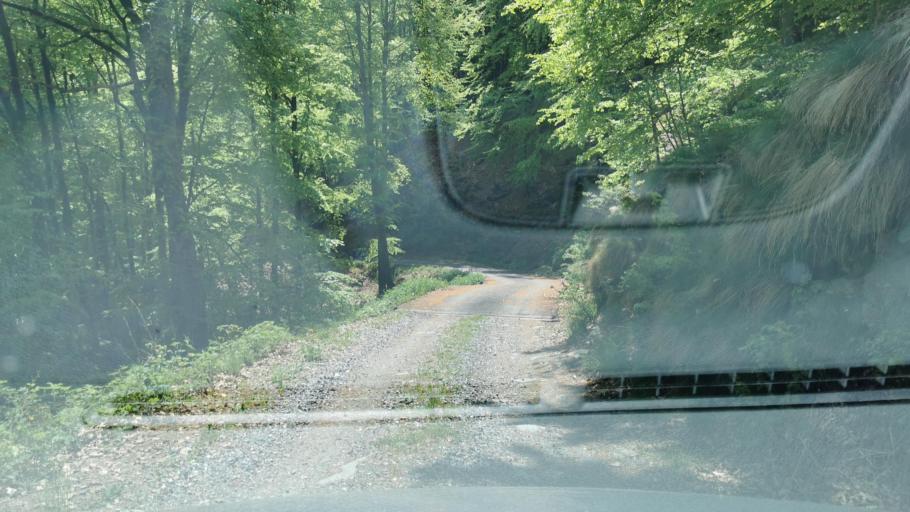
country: IT
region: Piedmont
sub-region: Provincia di Torino
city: Lemie
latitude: 45.2415
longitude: 7.2798
